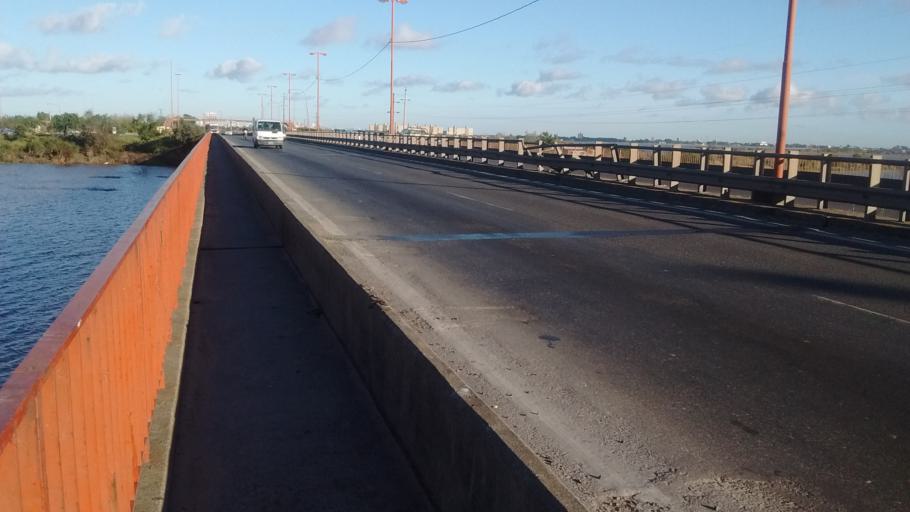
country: AR
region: Santa Fe
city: Santa Fe de la Vera Cruz
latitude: -31.6398
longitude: -60.6364
